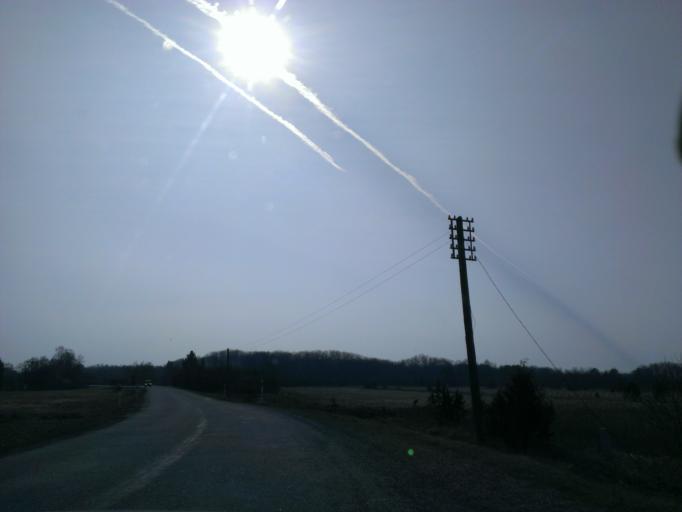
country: EE
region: Saare
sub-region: Orissaare vald
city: Orissaare
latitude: 58.5362
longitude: 23.1096
